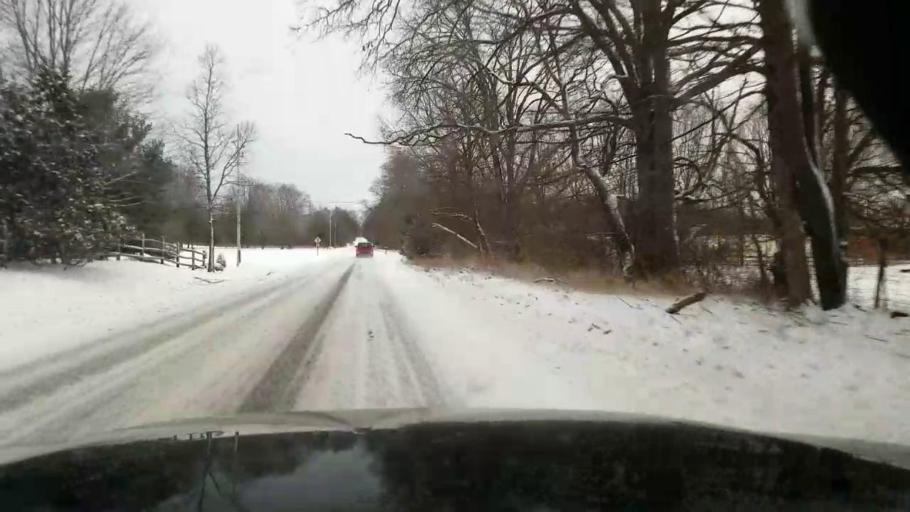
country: US
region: Michigan
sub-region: Jackson County
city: Spring Arbor
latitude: 42.1588
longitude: -84.4995
